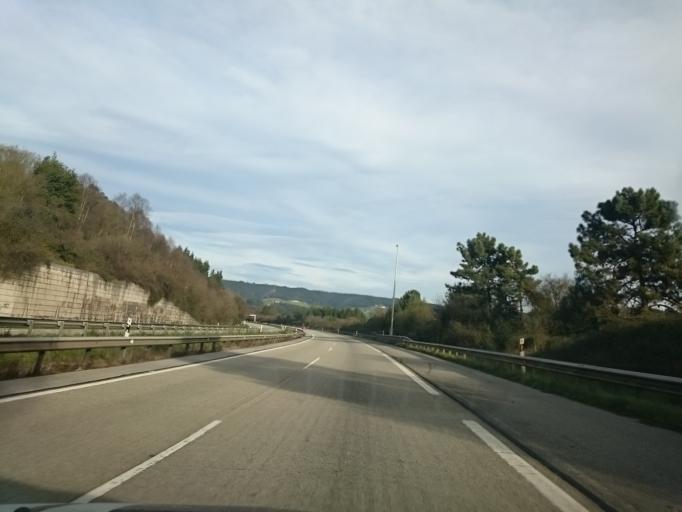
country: ES
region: Asturias
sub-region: Province of Asturias
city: Lugones
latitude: 43.4814
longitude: -5.7889
